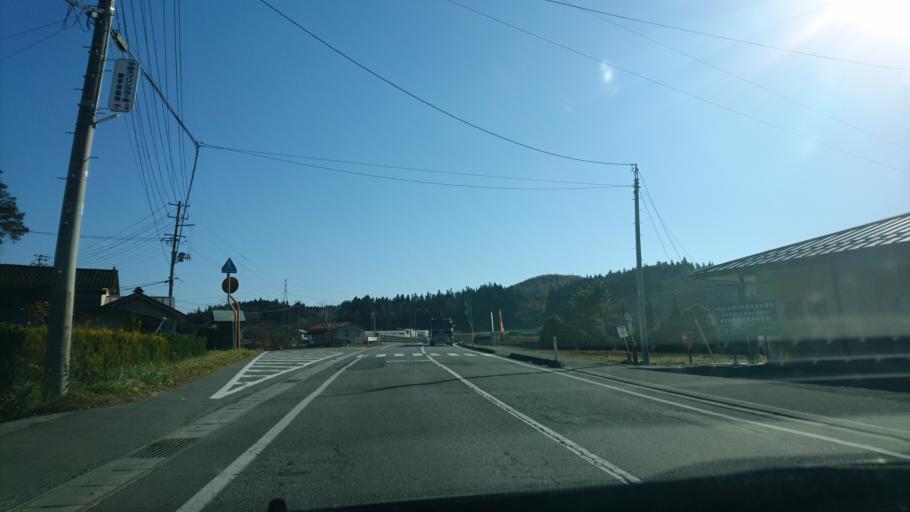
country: JP
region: Iwate
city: Ichinoseki
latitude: 38.9918
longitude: 141.2841
